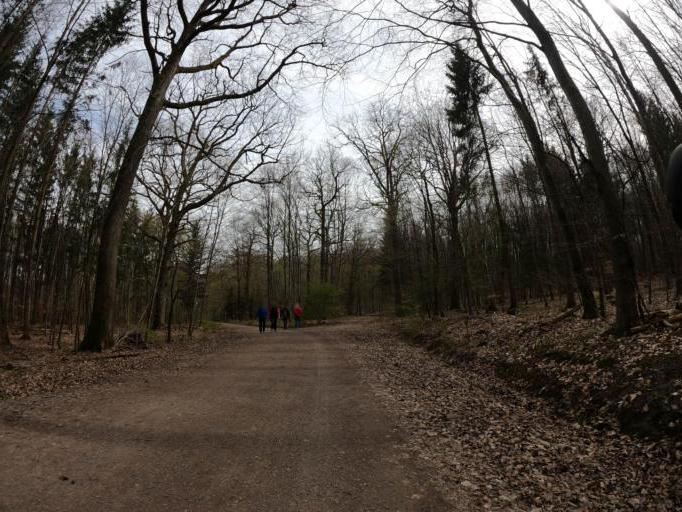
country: DE
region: Baden-Wuerttemberg
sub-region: Regierungsbezirk Stuttgart
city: Filderstadt
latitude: 48.6433
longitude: 9.2008
